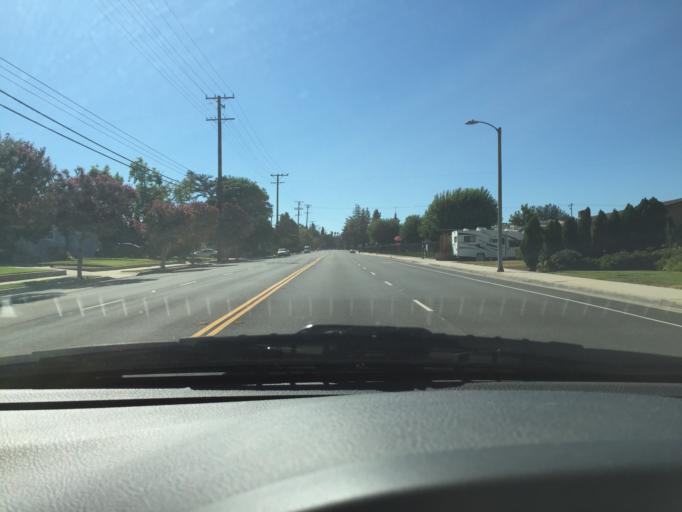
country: US
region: California
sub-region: San Bernardino County
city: Redlands
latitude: 34.0414
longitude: -117.1927
